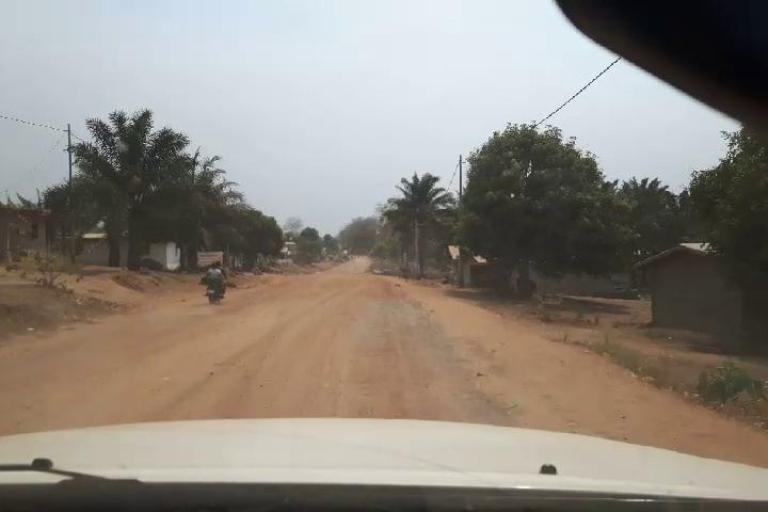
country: SL
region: Northern Province
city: Bumbuna
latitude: 9.0396
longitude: -11.7569
